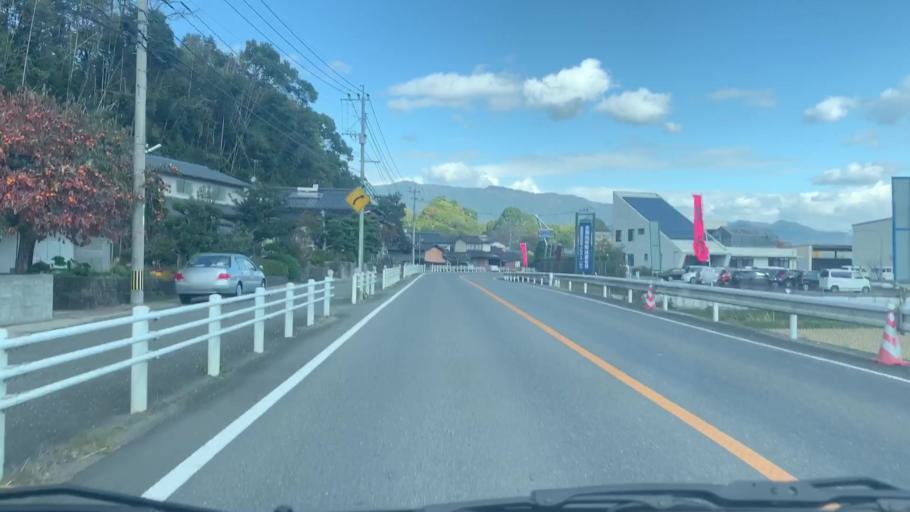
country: JP
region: Saga Prefecture
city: Saga-shi
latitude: 33.2696
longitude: 130.1806
